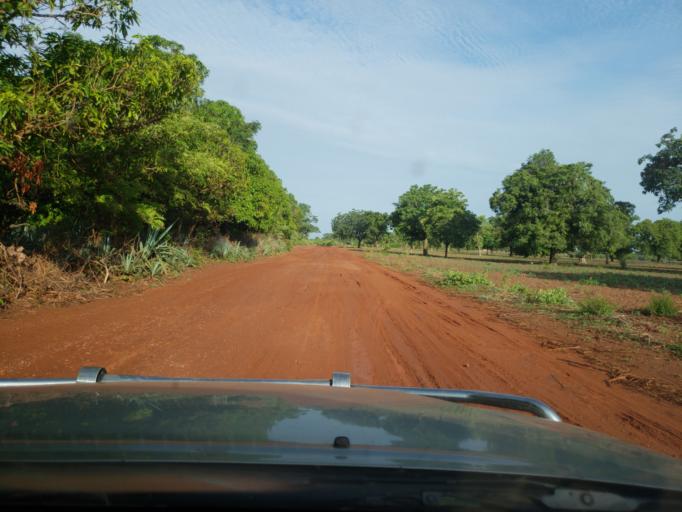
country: ML
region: Sikasso
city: Koutiala
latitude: 12.4244
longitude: -5.6615
